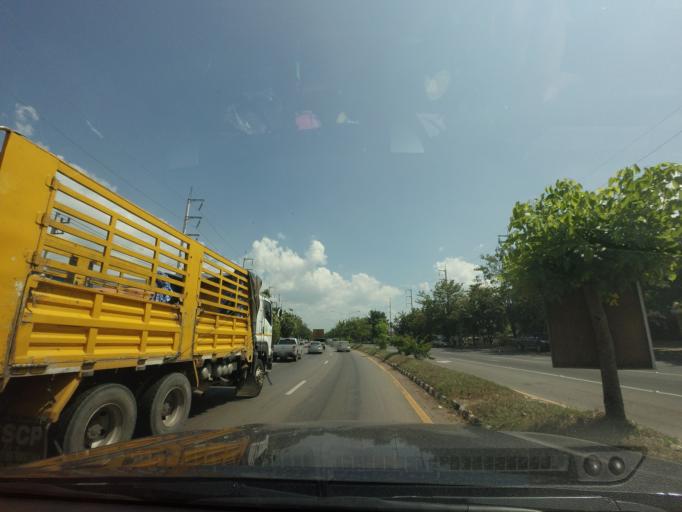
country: TH
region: Phetchabun
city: Nong Phai
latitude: 16.0809
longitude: 101.0585
